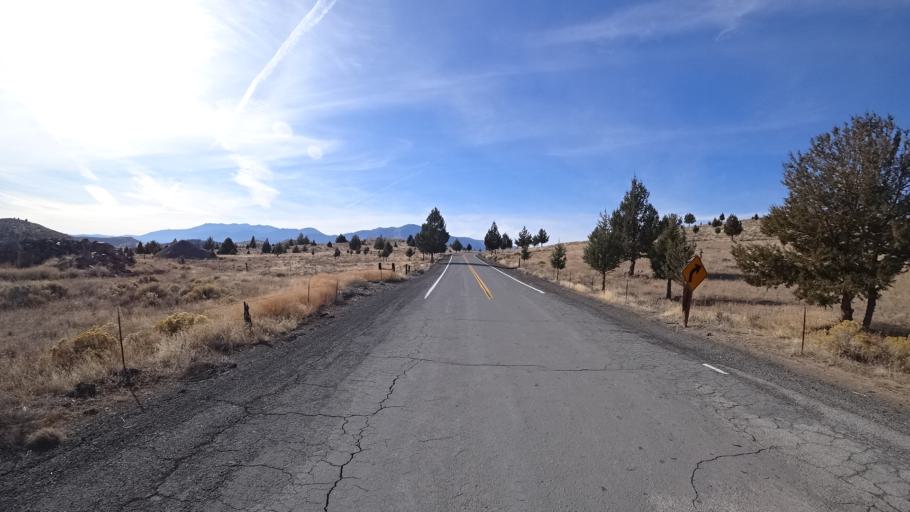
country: US
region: California
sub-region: Siskiyou County
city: Weed
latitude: 41.5545
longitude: -122.4740
